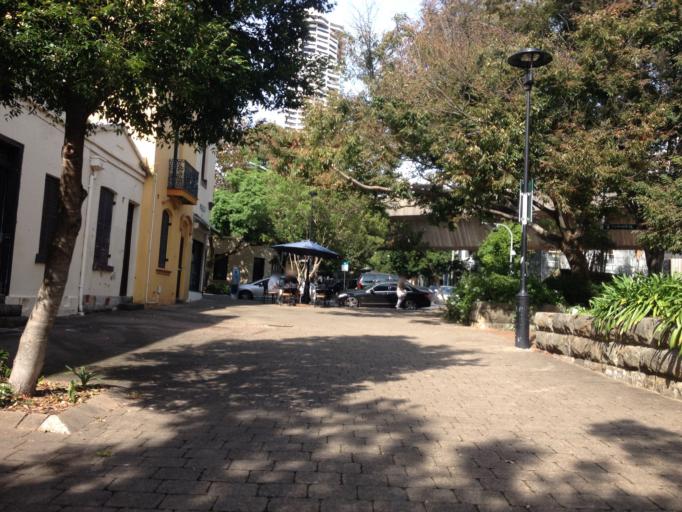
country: AU
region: New South Wales
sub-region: City of Sydney
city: Darlinghurst
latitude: -33.8725
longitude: 151.2197
